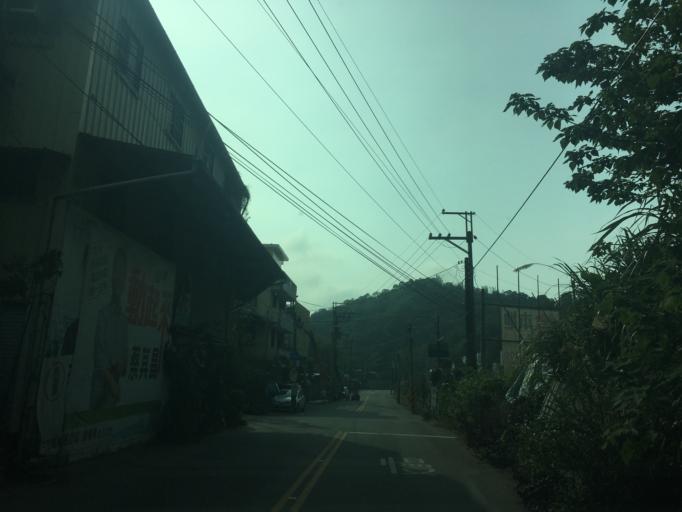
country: TW
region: Taiwan
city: Fengyuan
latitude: 24.2346
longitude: 120.7443
